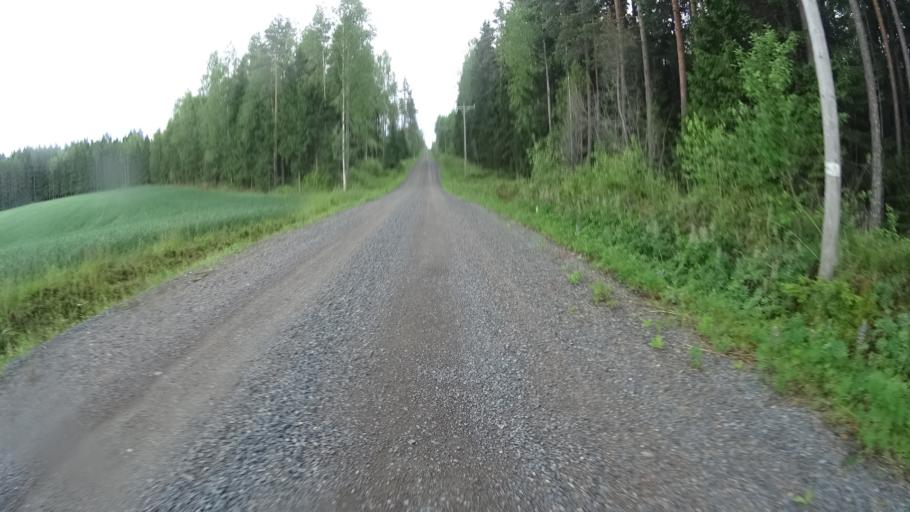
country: FI
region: Uusimaa
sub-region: Helsinki
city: Karkkila
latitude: 60.5901
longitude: 24.1611
